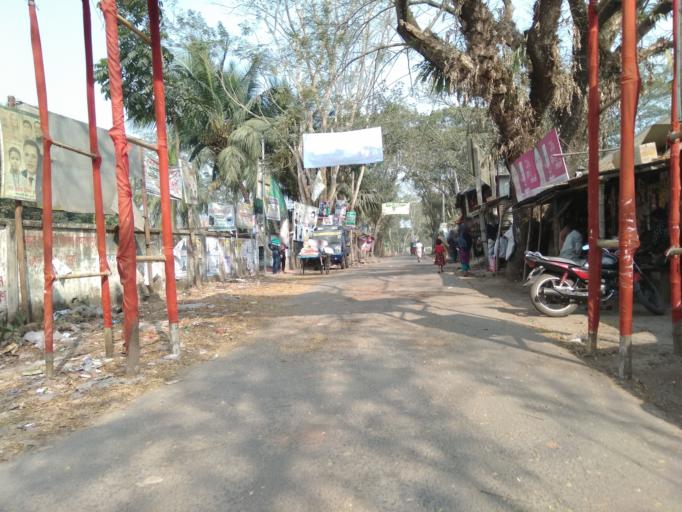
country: BD
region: Barisal
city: Mehendiganj
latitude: 22.9563
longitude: 90.4147
